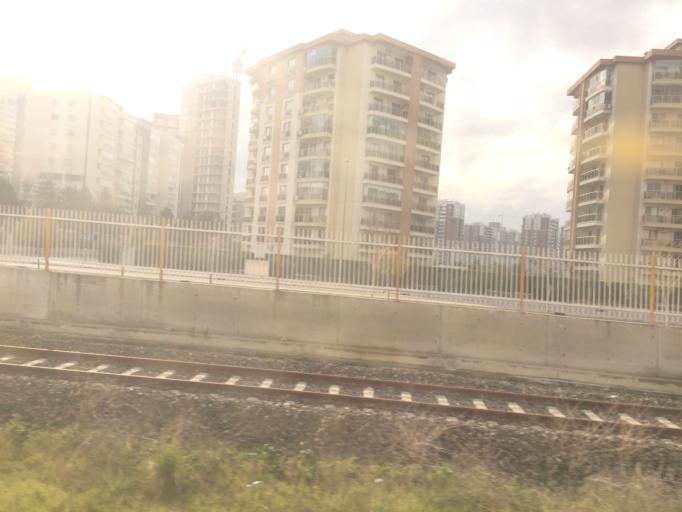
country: TR
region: Izmir
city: Karsiyaka
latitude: 38.4808
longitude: 27.0840
